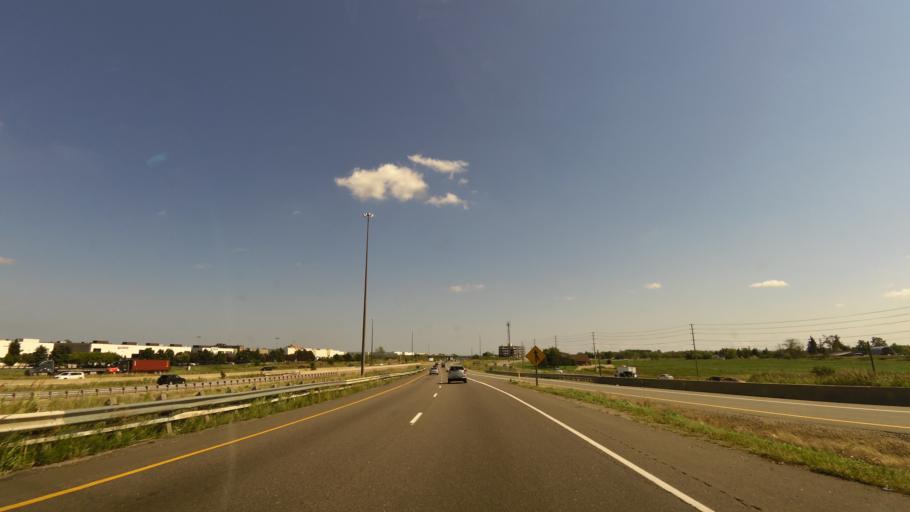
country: CA
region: Ontario
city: Mississauga
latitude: 43.5252
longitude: -79.7216
